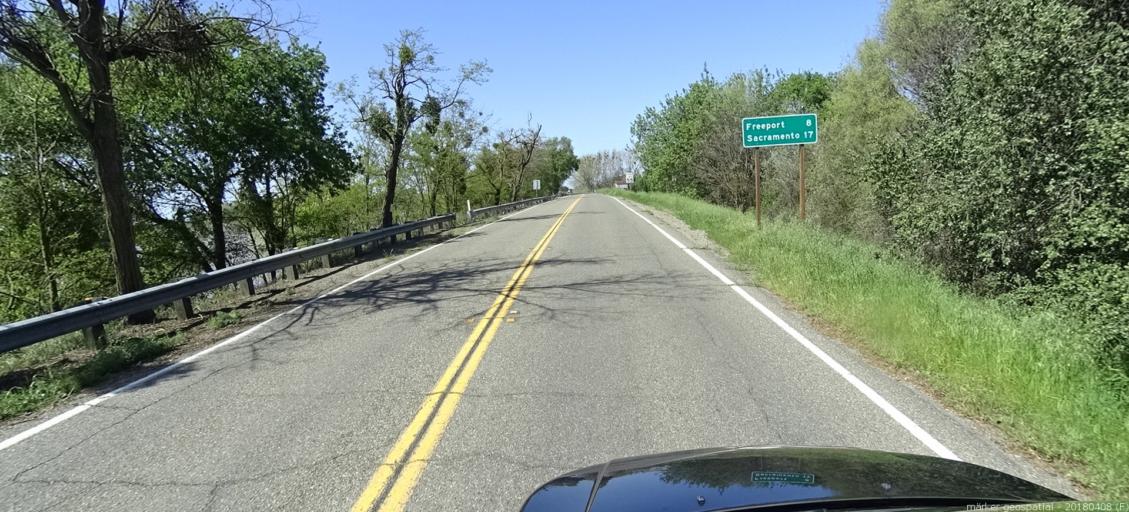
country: US
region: California
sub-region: Sacramento County
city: Laguna
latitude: 38.3701
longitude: -121.5207
